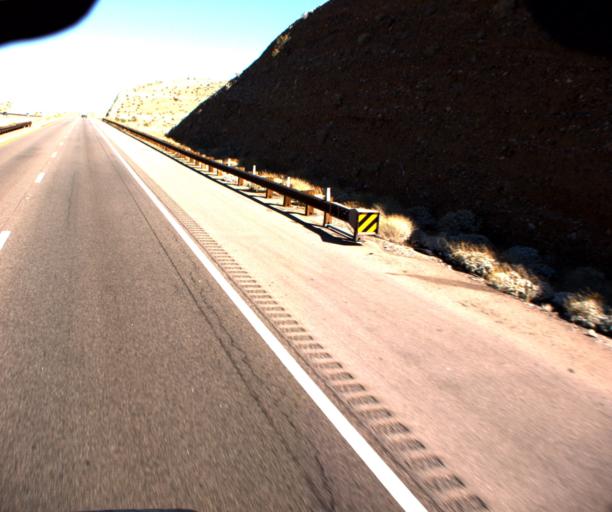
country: US
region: Nevada
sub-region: Clark County
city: Boulder City
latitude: 35.8894
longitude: -114.6216
